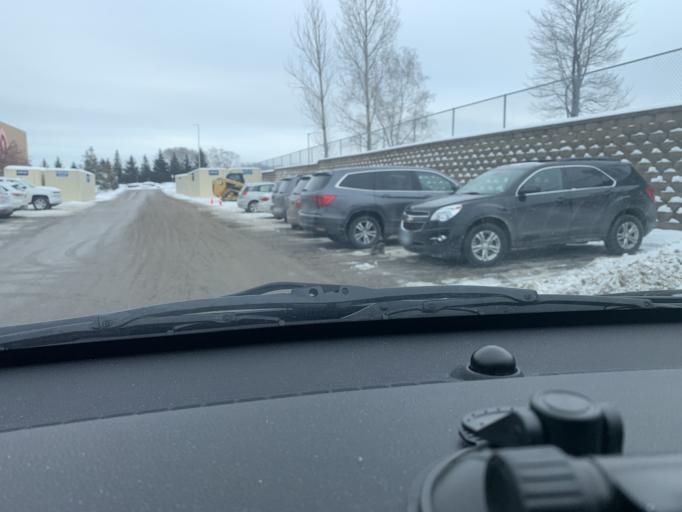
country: US
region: Minnesota
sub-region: Dakota County
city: West Saint Paul
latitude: 44.8924
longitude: -93.0785
